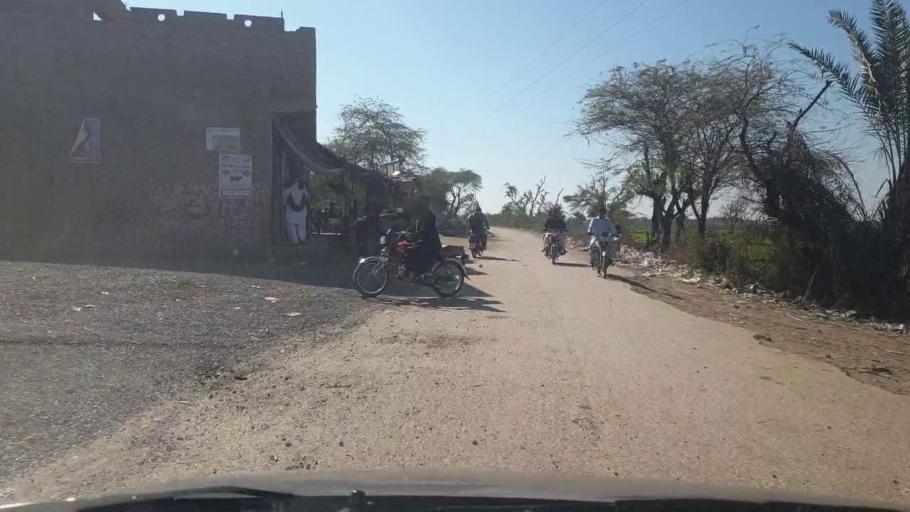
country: PK
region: Sindh
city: Bozdar
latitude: 27.0954
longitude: 68.6257
